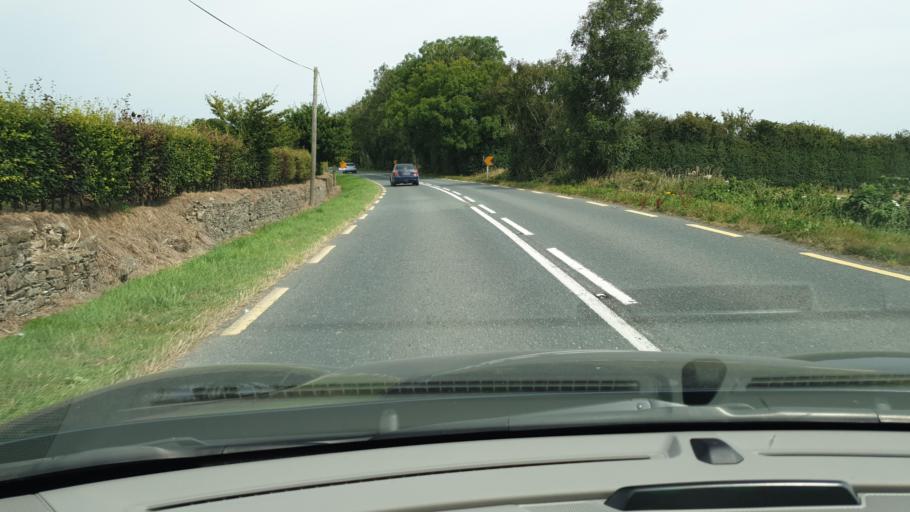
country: IE
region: Leinster
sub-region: An Mhi
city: Kells
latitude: 53.7015
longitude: -6.9186
